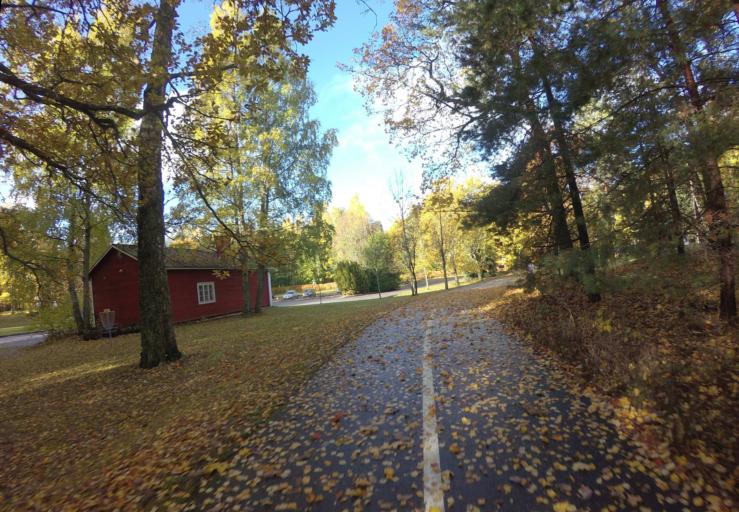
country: FI
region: Varsinais-Suomi
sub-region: Turku
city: Raisio
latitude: 60.4260
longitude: 22.1042
